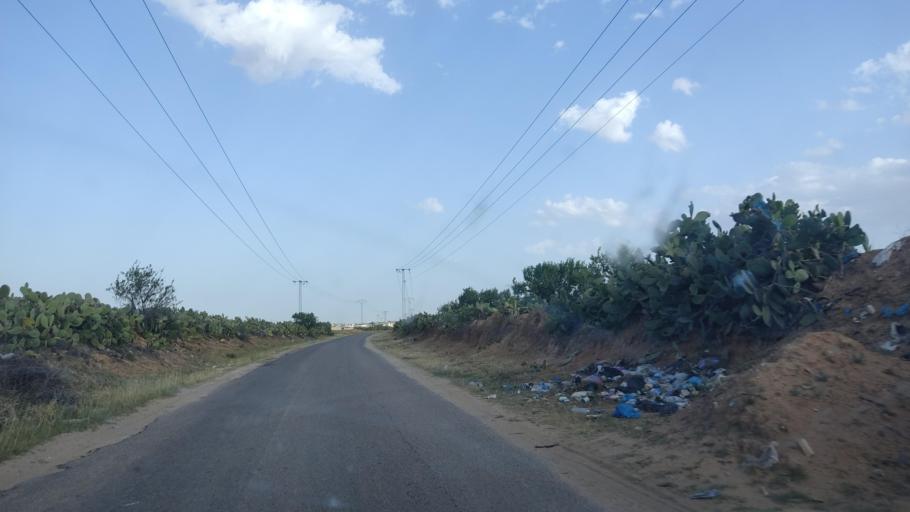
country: TN
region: Safaqis
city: Sfax
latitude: 34.8542
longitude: 10.6078
